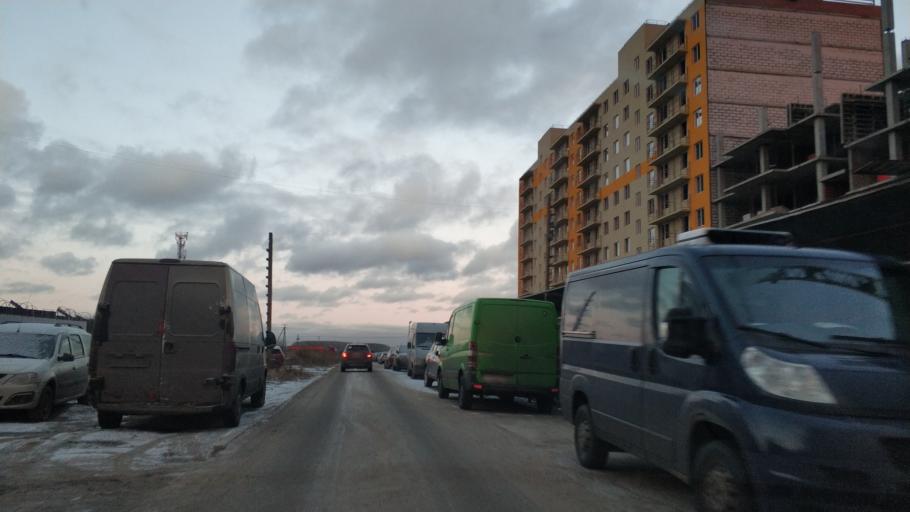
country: RU
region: St.-Petersburg
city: Pontonnyy
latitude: 59.7993
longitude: 30.6327
